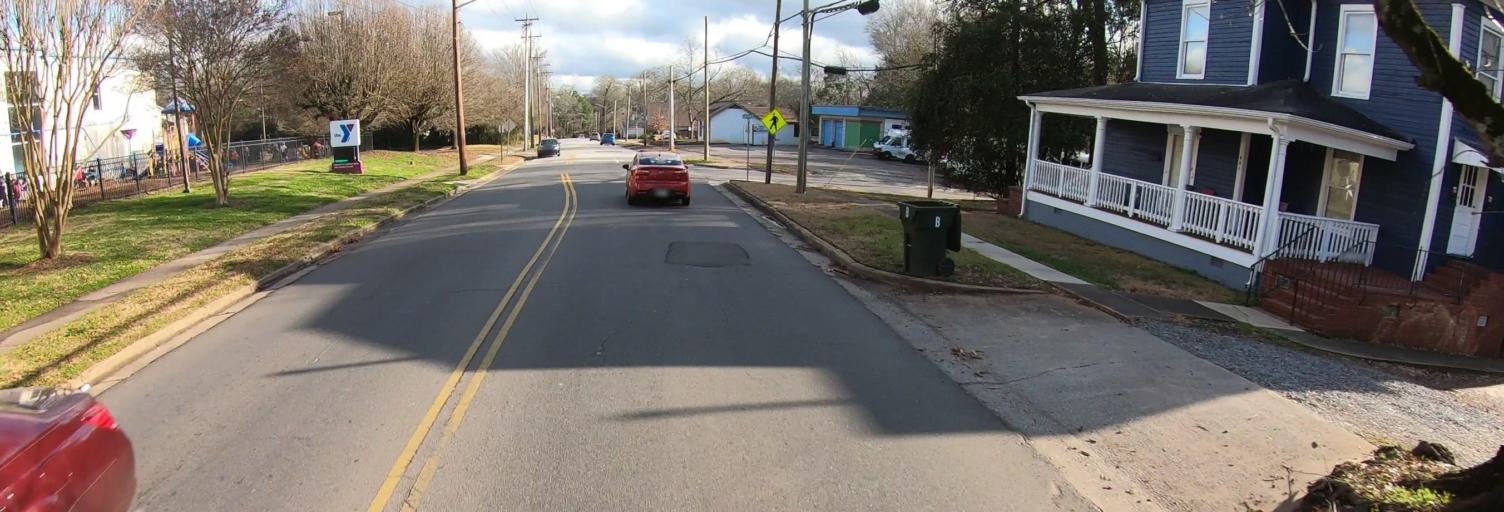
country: US
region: South Carolina
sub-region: York County
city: Rock Hill
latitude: 34.9365
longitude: -81.0243
